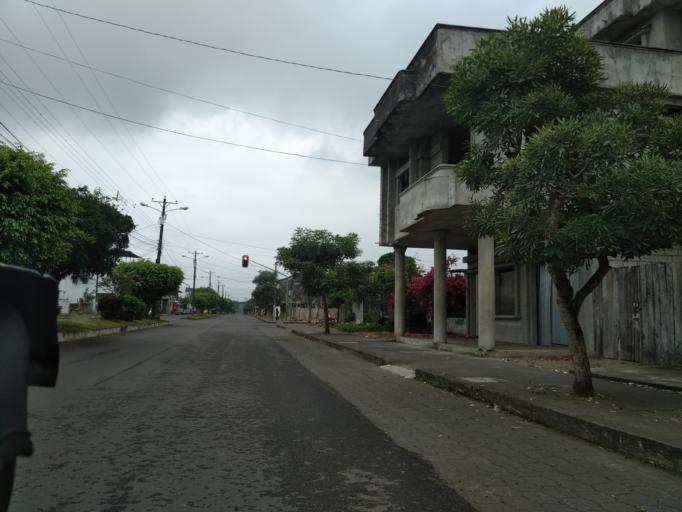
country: EC
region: Cotopaxi
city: La Mana
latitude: -0.9538
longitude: -79.3508
